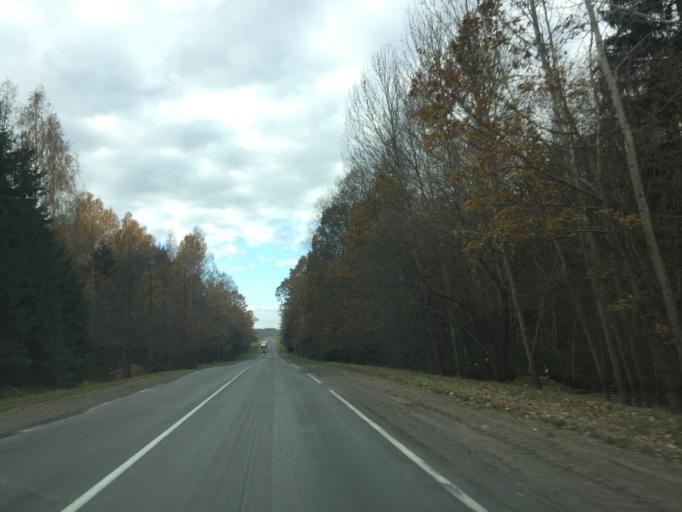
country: BY
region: Vitebsk
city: Mosar
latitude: 55.0630
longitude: 27.2669
